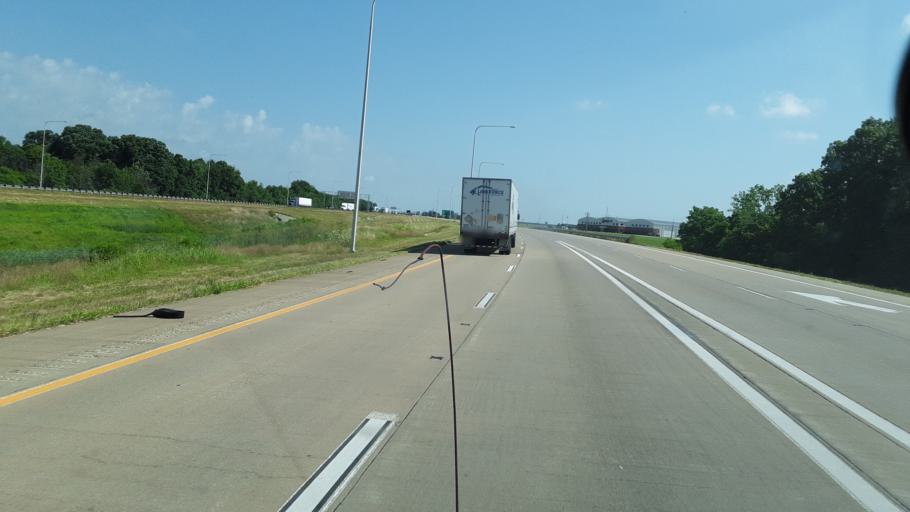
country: US
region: Illinois
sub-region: Effingham County
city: Effingham
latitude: 39.0990
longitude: -88.5756
